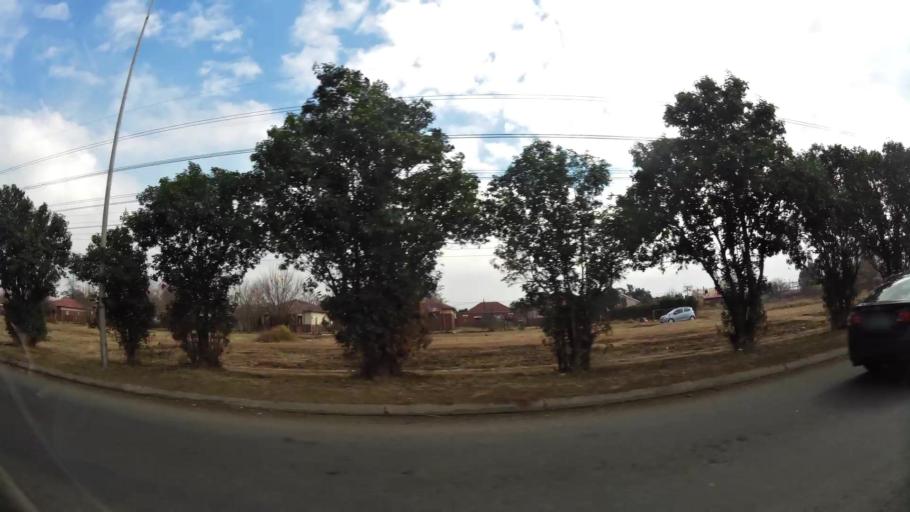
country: ZA
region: Gauteng
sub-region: Sedibeng District Municipality
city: Vereeniging
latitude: -26.6739
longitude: 27.9384
